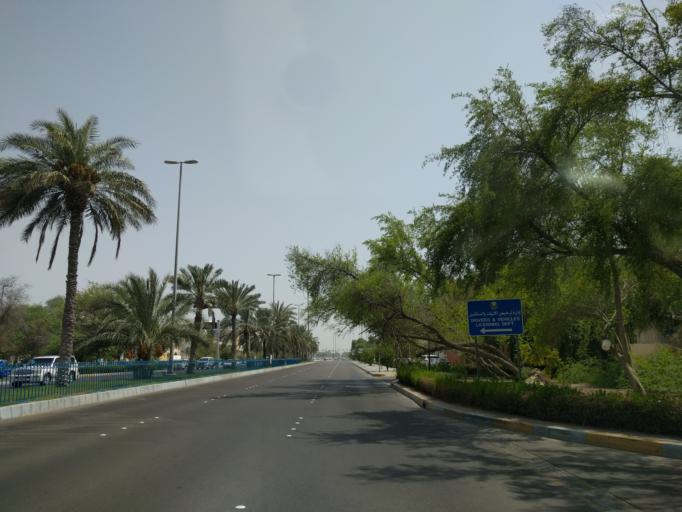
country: AE
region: Abu Dhabi
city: Abu Dhabi
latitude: 24.4413
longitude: 54.4178
